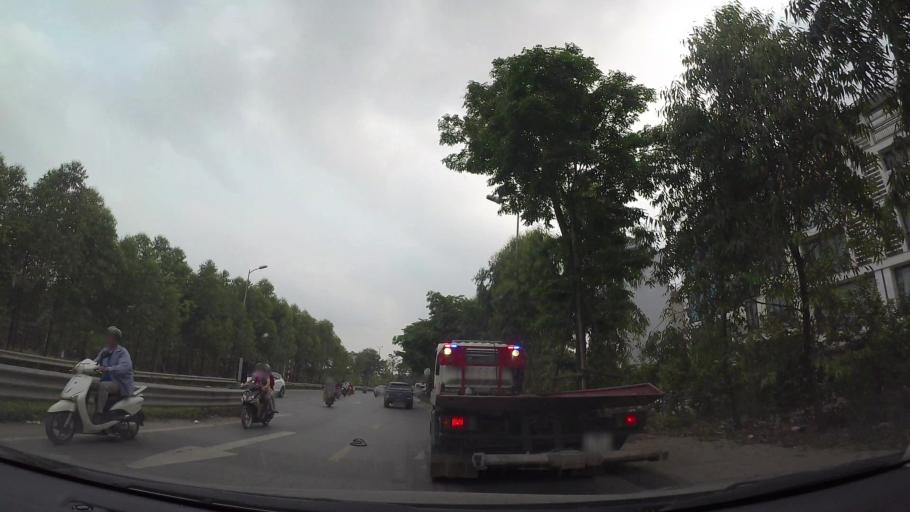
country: VN
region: Ha Noi
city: Trau Quy
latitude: 21.0067
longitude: 105.9120
